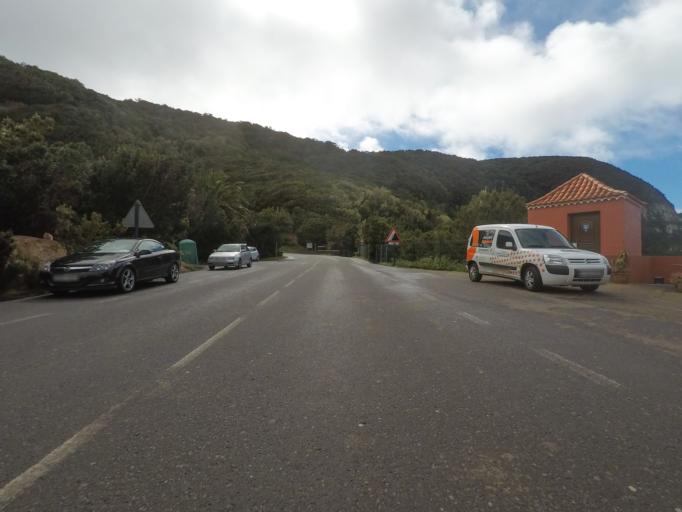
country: ES
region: Canary Islands
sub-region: Provincia de Santa Cruz de Tenerife
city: Vallehermosa
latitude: 28.1644
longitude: -17.2973
